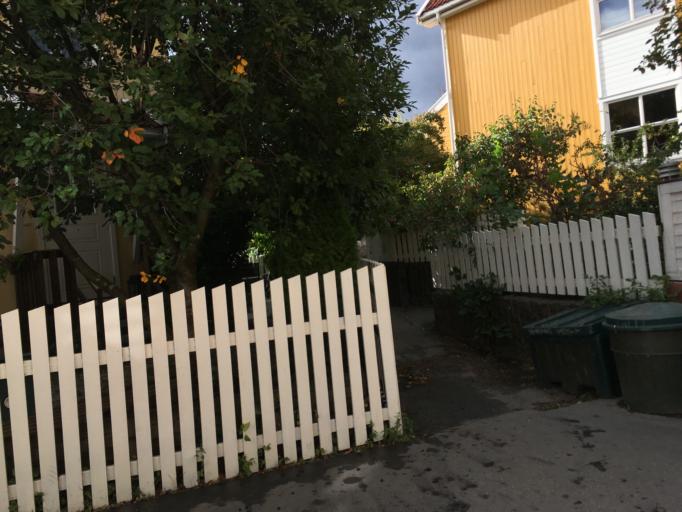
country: NO
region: Oslo
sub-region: Oslo
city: Oslo
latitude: 59.9122
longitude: 10.7858
